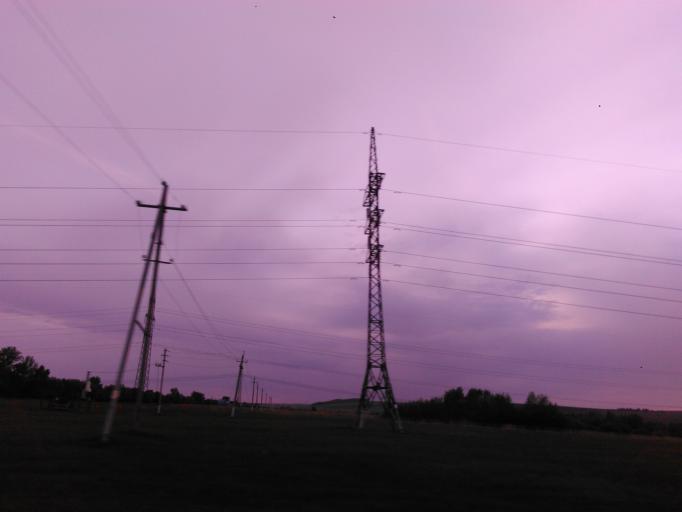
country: RU
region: Tatarstan
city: Russkiy Aktash
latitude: 55.1067
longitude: 52.0475
